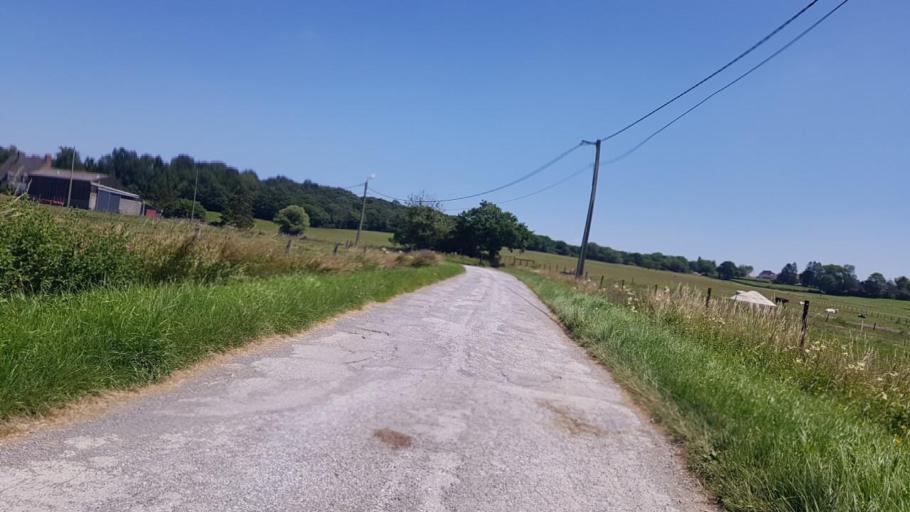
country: BE
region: Wallonia
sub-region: Province du Hainaut
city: Froidchapelle
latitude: 50.1467
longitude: 4.2696
